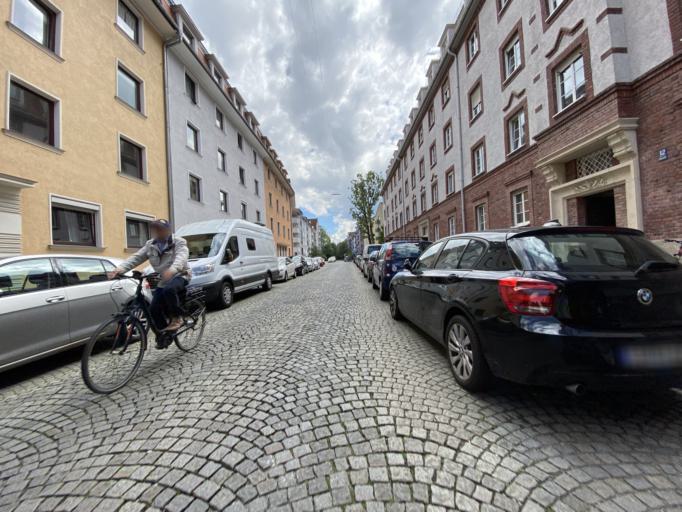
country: DE
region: Bavaria
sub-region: Upper Bavaria
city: Munich
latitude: 48.1382
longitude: 11.5177
